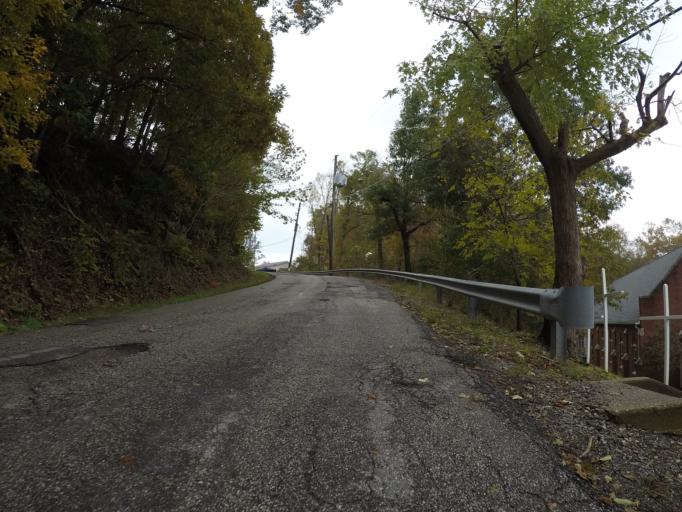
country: US
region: West Virginia
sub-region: Wayne County
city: Lavalette
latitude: 38.3650
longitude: -82.4202
